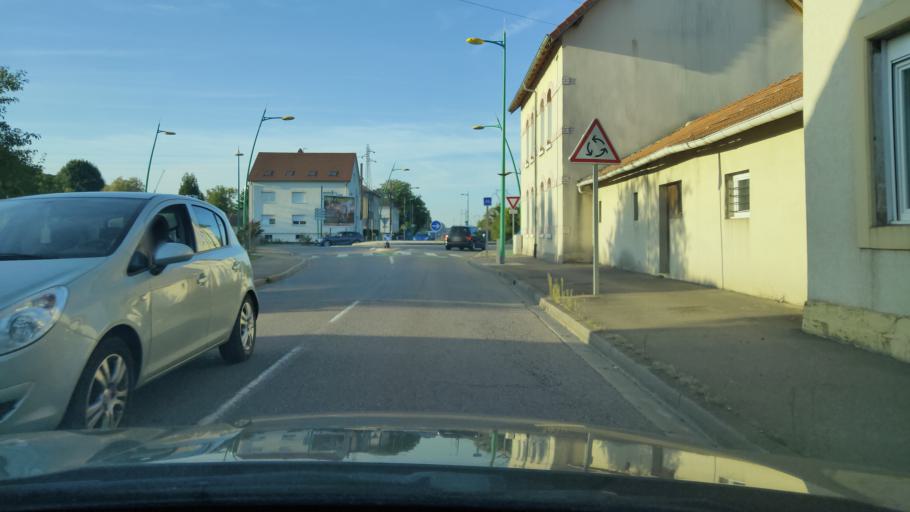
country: FR
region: Lorraine
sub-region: Departement de la Moselle
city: Maizieres-les-Metz
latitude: 49.2103
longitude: 6.1483
